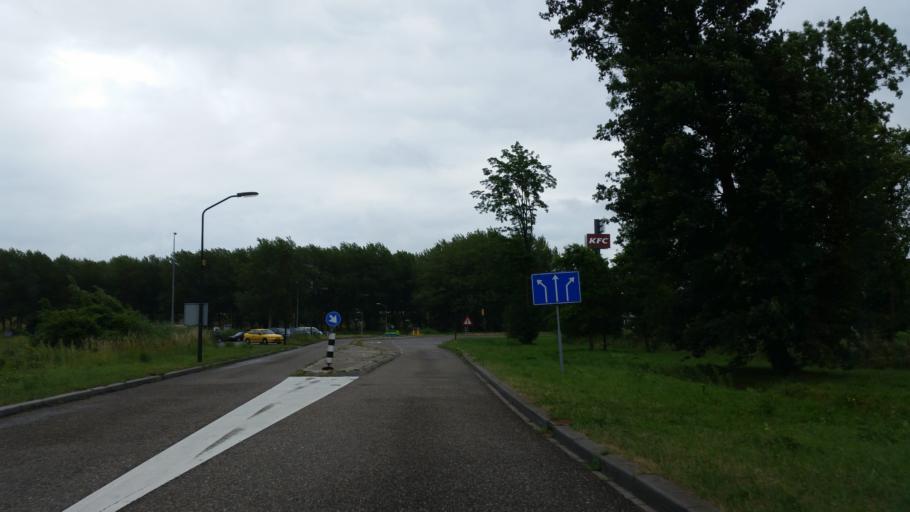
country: NL
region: Flevoland
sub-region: Gemeente Lelystad
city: Lelystad
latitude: 52.4827
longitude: 5.5013
